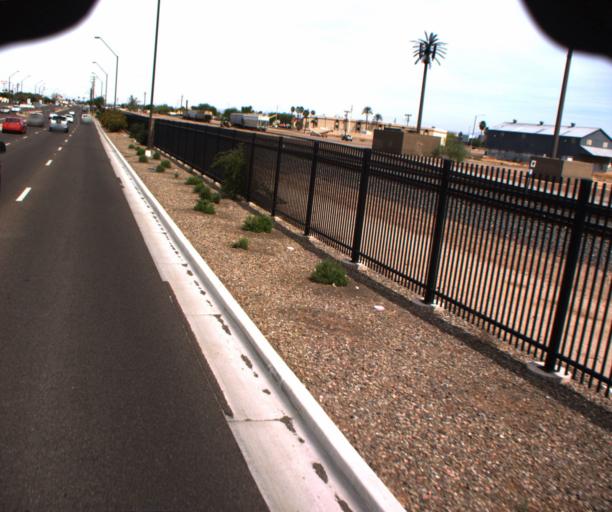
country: US
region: Arizona
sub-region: Maricopa County
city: Peoria
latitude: 33.5781
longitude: -112.2336
